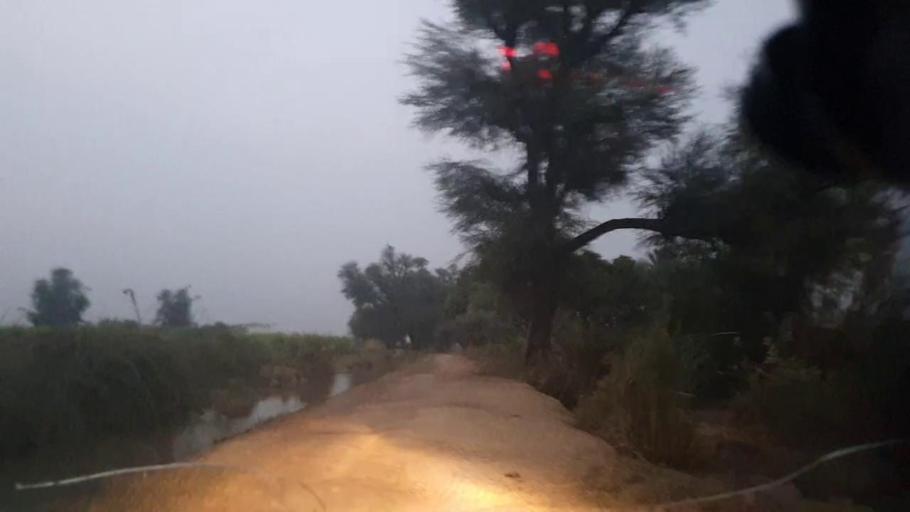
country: PK
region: Sindh
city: Hingorja
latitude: 27.1995
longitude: 68.3716
